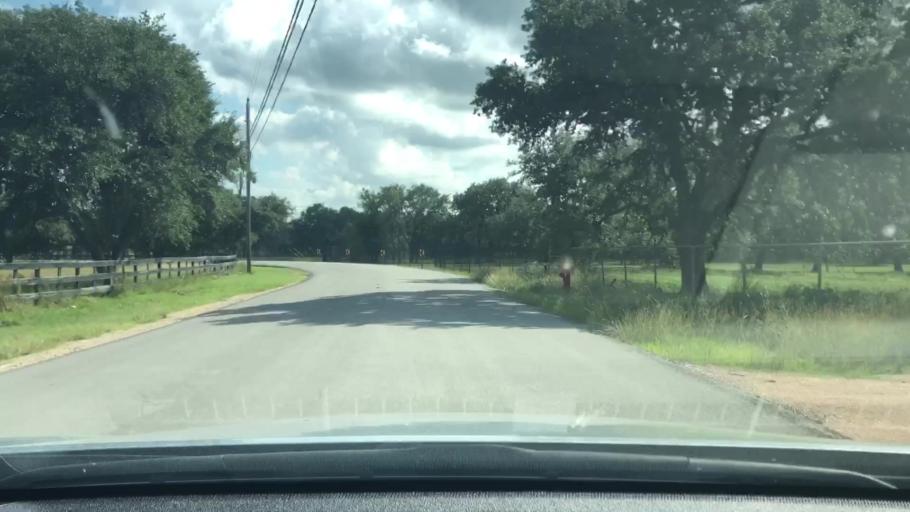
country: US
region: Texas
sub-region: Bexar County
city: Fair Oaks Ranch
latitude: 29.7644
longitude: -98.6305
